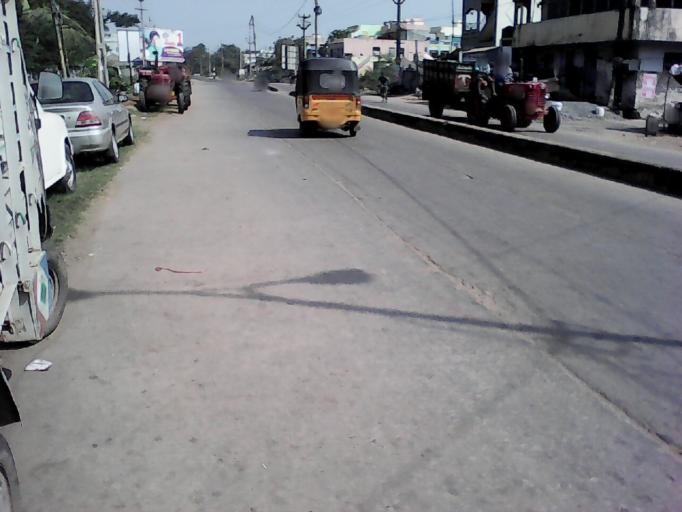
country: IN
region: Andhra Pradesh
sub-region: Guntur
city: Bhattiprolu
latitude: 16.2371
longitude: 80.6595
